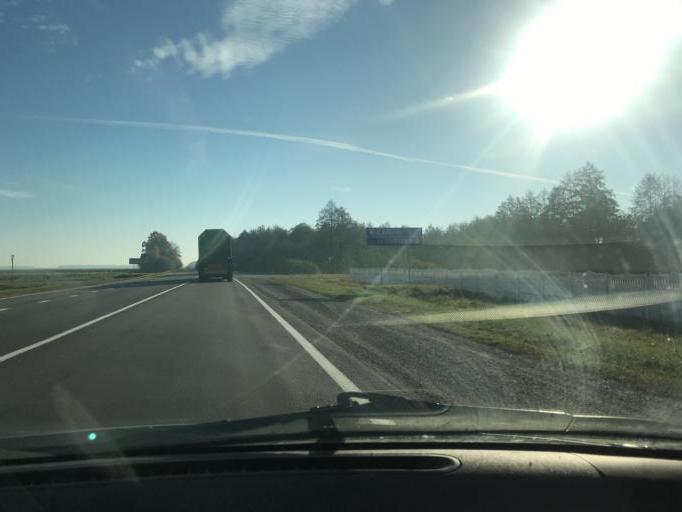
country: BY
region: Brest
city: Ivanava
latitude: 52.1497
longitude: 25.3935
